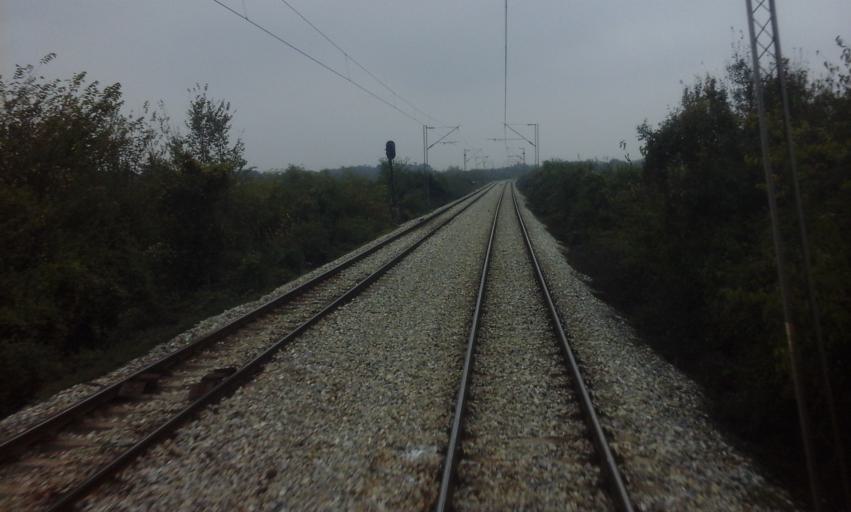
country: RS
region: Central Serbia
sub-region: Sumadijski Okrug
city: Lapovo
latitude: 44.2206
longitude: 21.0950
